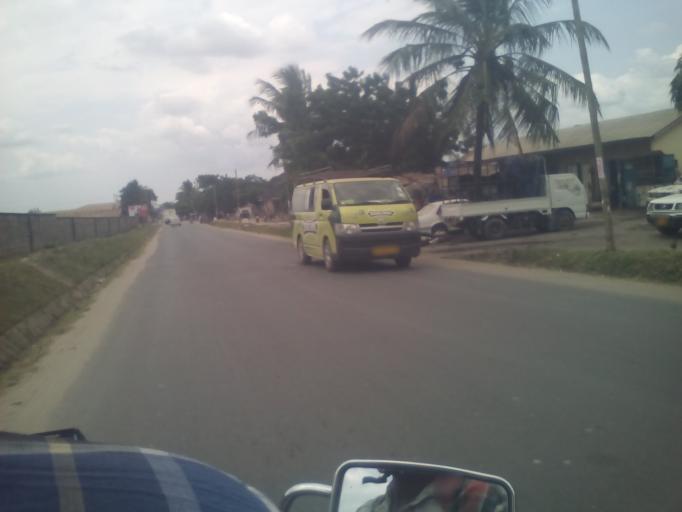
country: TZ
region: Dar es Salaam
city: Dar es Salaam
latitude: -6.8628
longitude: 39.2207
